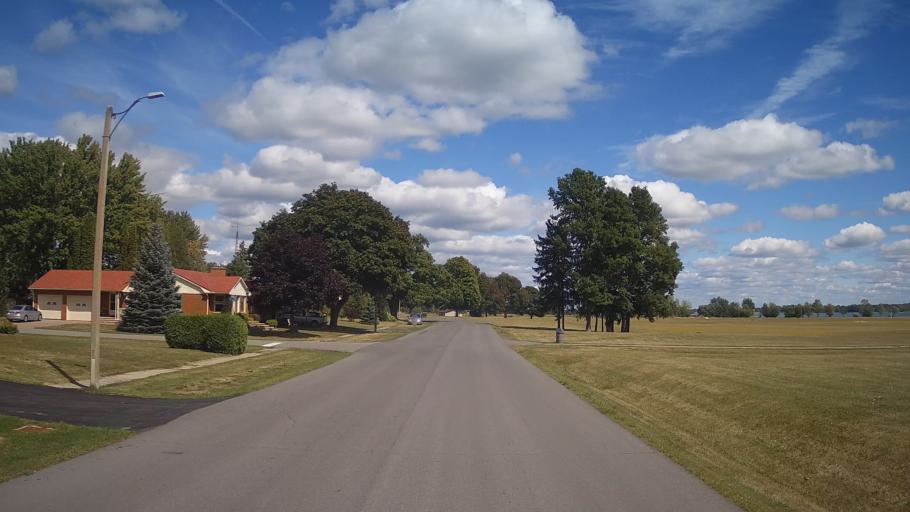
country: US
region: New York
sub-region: St. Lawrence County
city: Ogdensburg
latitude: 44.8419
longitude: -75.3167
